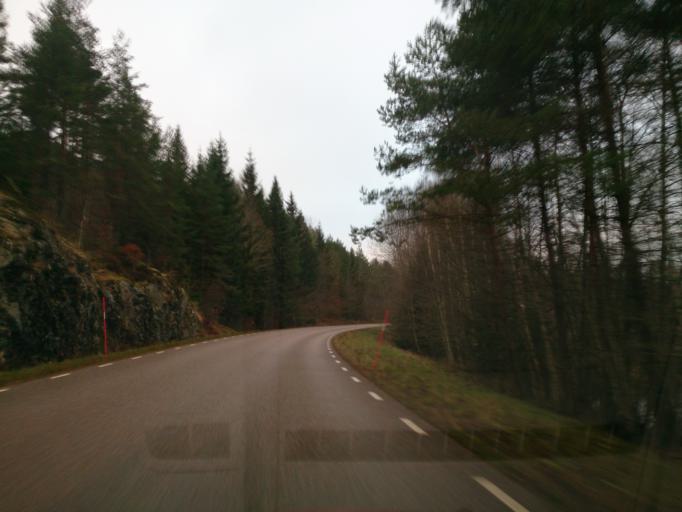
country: SE
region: OEstergoetland
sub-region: Atvidabergs Kommun
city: Atvidaberg
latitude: 58.2374
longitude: 16.0063
